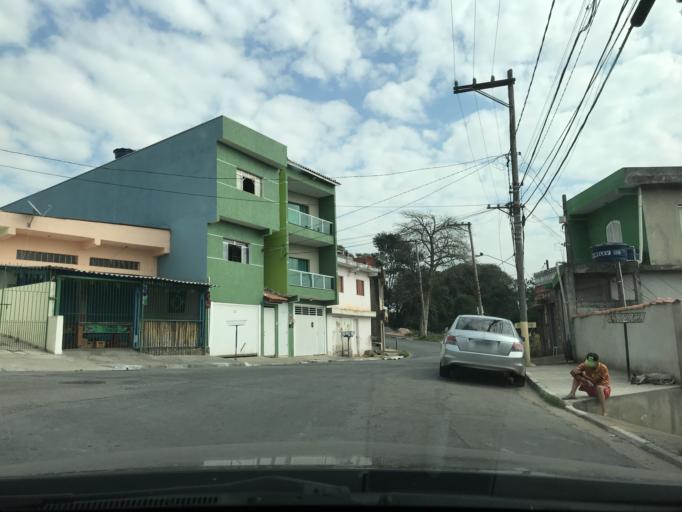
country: BR
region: Sao Paulo
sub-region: Cotia
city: Cotia
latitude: -23.6207
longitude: -46.9276
